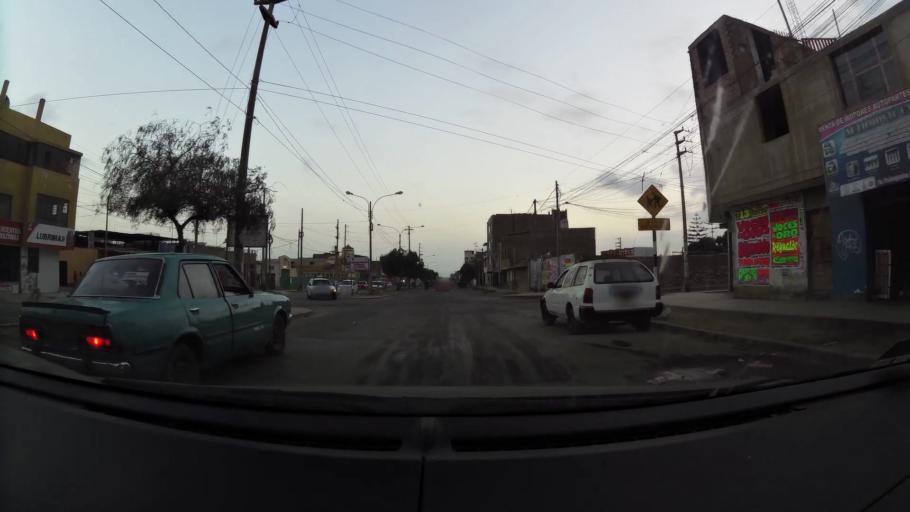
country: PE
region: La Libertad
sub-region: Provincia de Trujillo
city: El Porvenir
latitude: -8.0876
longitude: -79.0155
